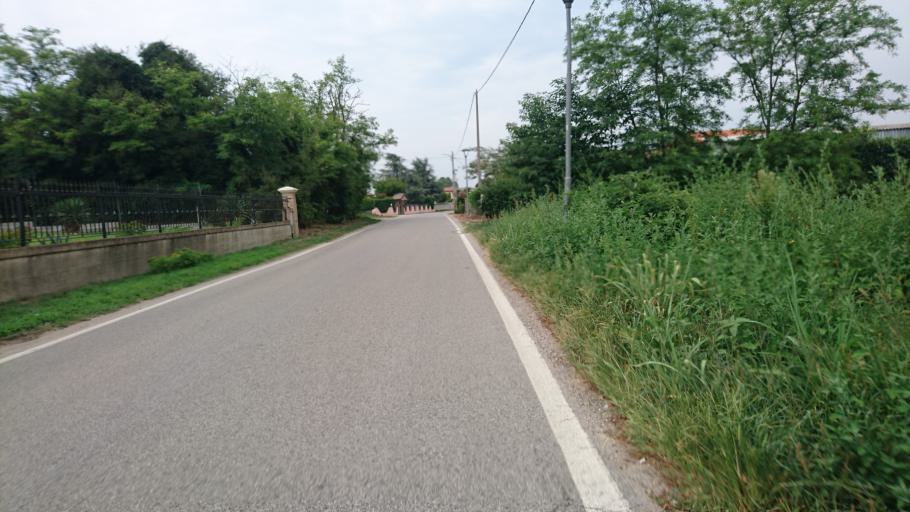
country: IT
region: Veneto
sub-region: Provincia di Rovigo
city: Rosolina
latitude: 45.0911
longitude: 12.2387
